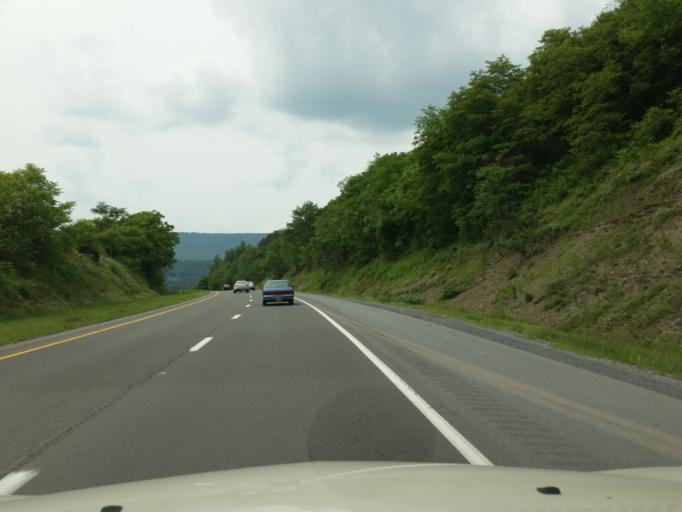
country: US
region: Pennsylvania
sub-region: Juniata County
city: Mifflintown
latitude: 40.5942
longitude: -77.3773
